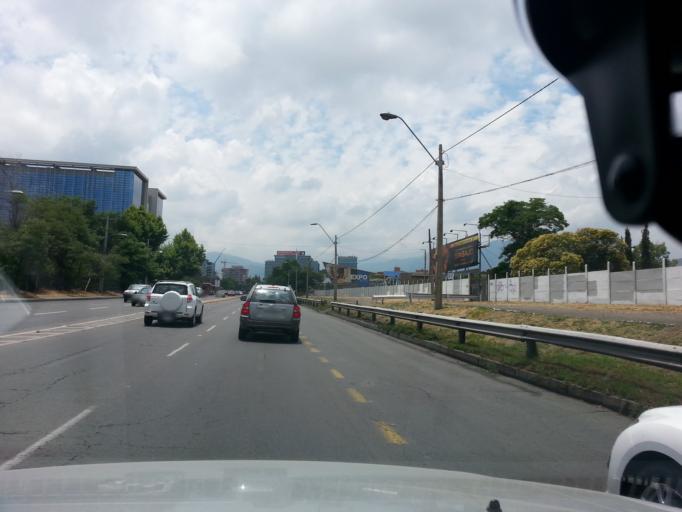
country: CL
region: Santiago Metropolitan
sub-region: Provincia de Santiago
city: Villa Presidente Frei, Nunoa, Santiago, Chile
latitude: -33.3812
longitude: -70.5313
